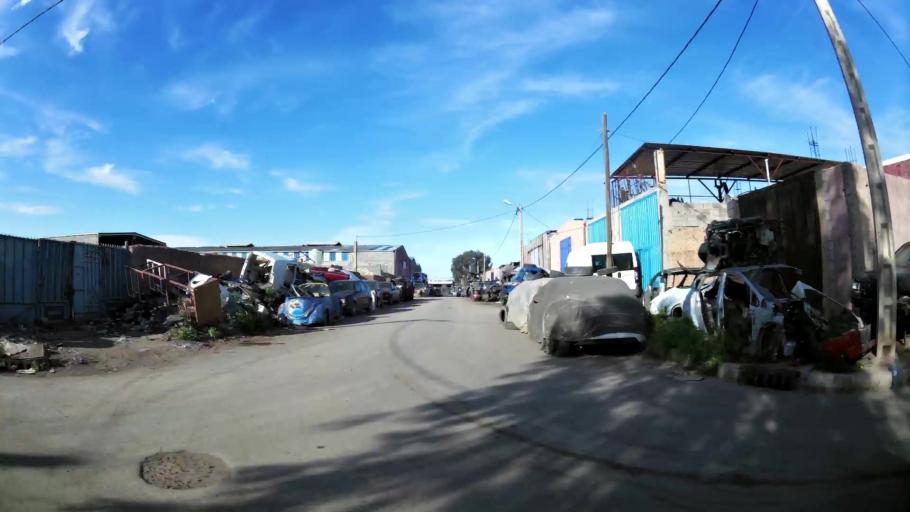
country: MA
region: Marrakech-Tensift-Al Haouz
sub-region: Marrakech
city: Marrakesh
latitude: 31.6822
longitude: -8.0550
